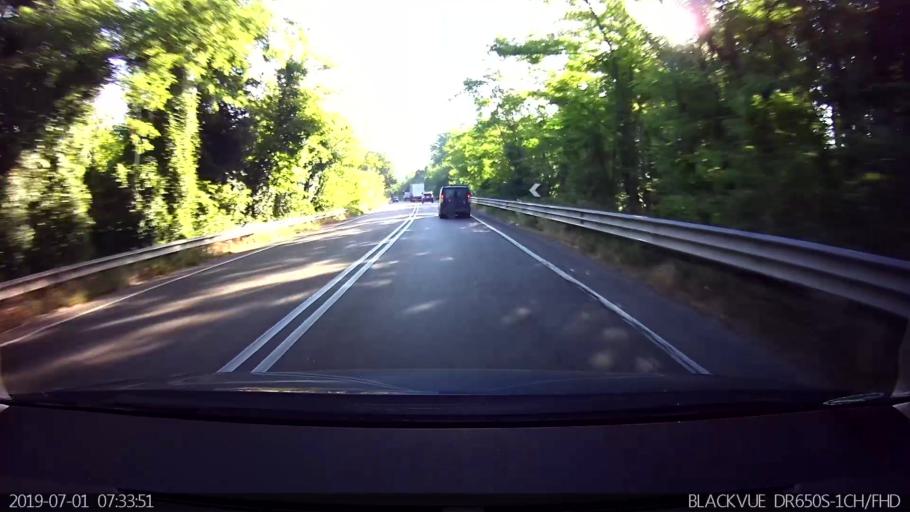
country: IT
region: Latium
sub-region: Provincia di Latina
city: Prossedi
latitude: 41.5111
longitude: 13.2669
